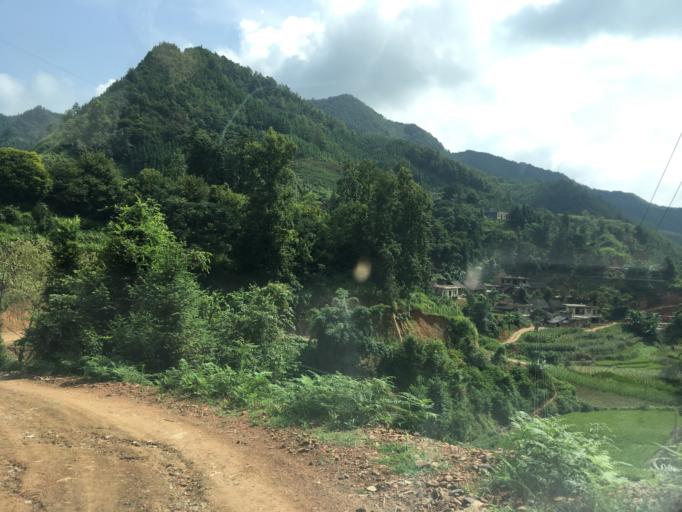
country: CN
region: Guangxi Zhuangzu Zizhiqu
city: Xinzhou
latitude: 24.8675
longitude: 105.8585
